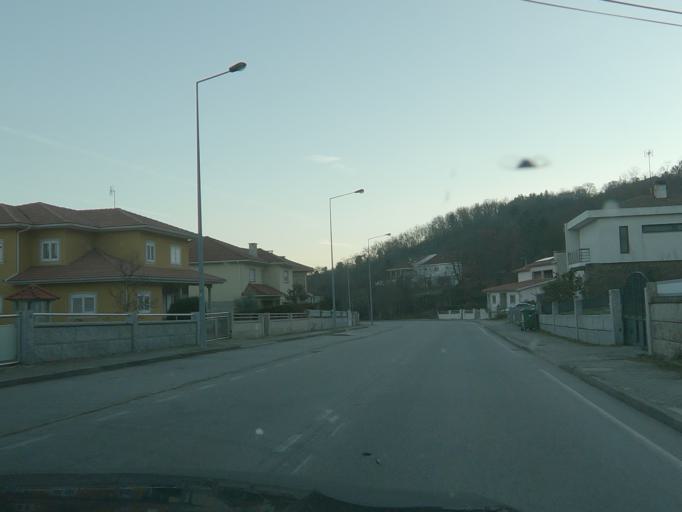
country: PT
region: Vila Real
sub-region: Vila Pouca de Aguiar
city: Vila Pouca de Aguiar
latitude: 41.4954
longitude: -7.6495
